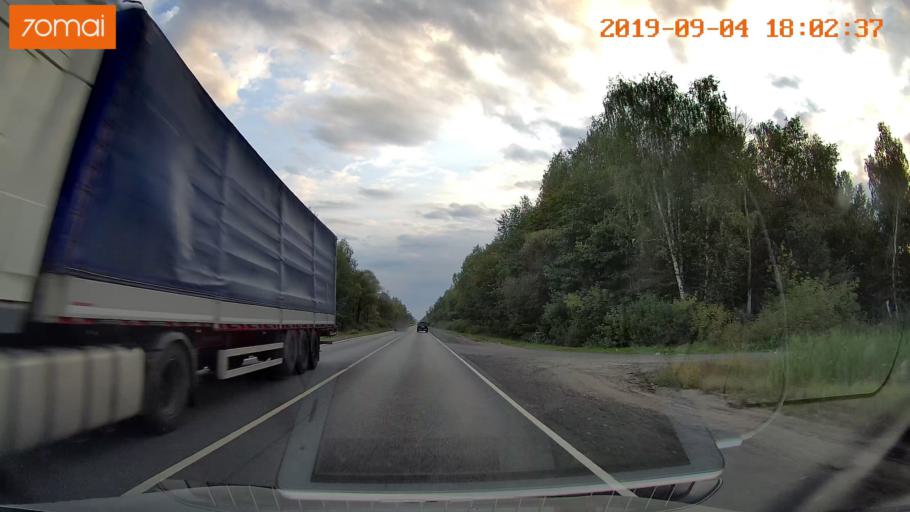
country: RU
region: Moskovskaya
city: Il'inskiy Pogost
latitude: 55.4723
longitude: 38.8626
